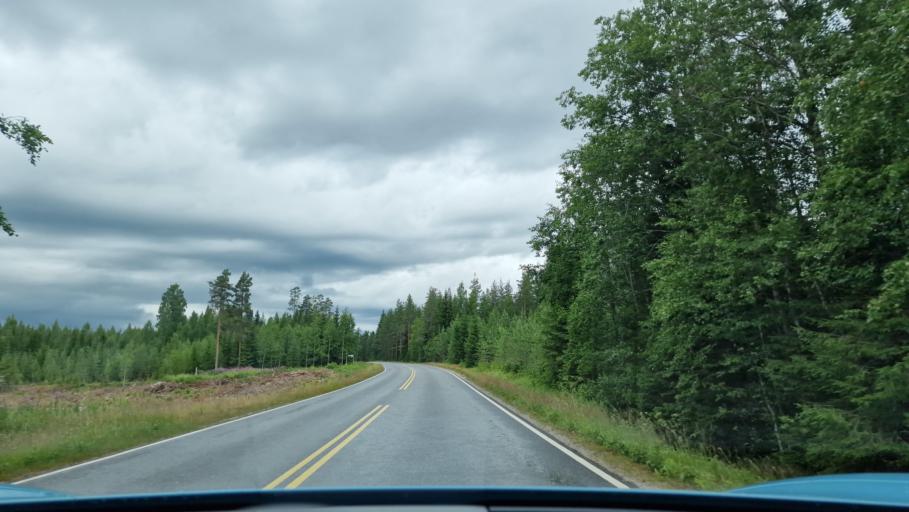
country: FI
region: Southern Ostrobothnia
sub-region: Jaerviseutu
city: Soini
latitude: 62.7047
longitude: 24.4519
